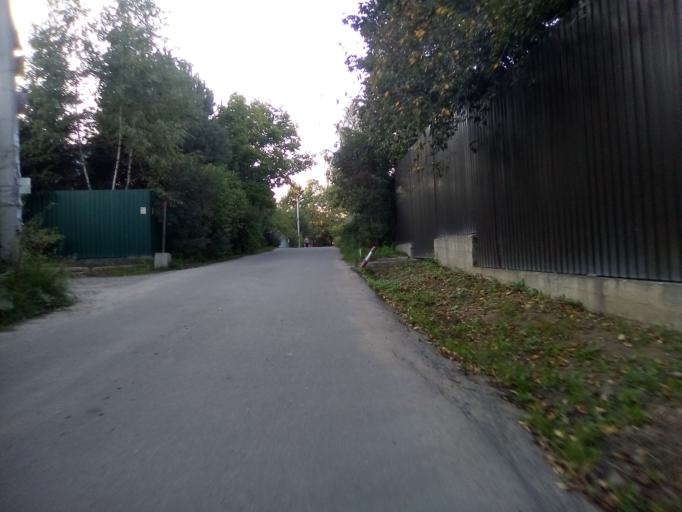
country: RU
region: Moskovskaya
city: Krasnoznamensk
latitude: 55.5758
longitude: 37.0369
